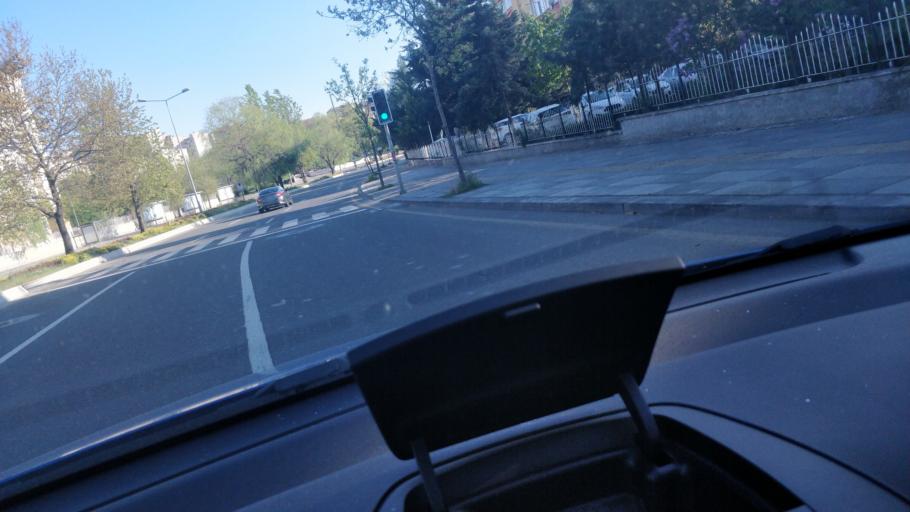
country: TR
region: Ankara
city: Batikent
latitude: 39.9652
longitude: 32.7335
